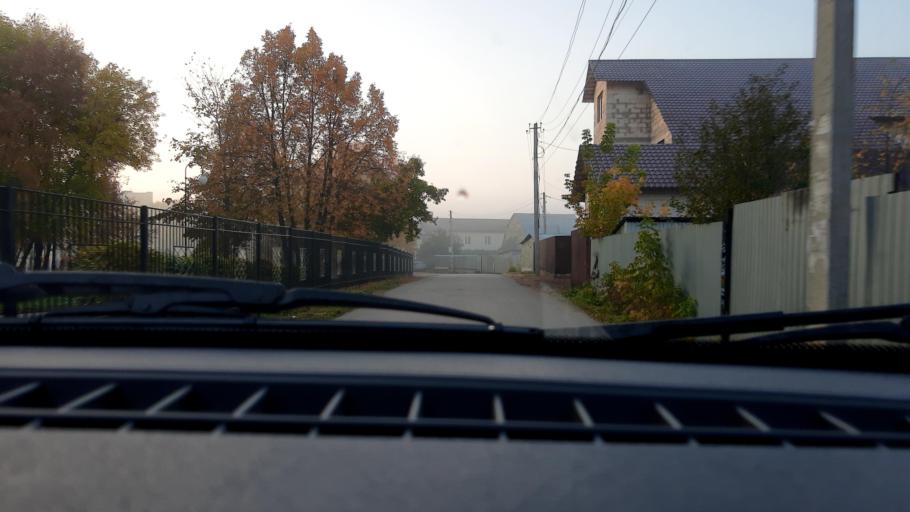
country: RU
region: Bashkortostan
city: Mikhaylovka
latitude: 54.7897
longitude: 55.8738
